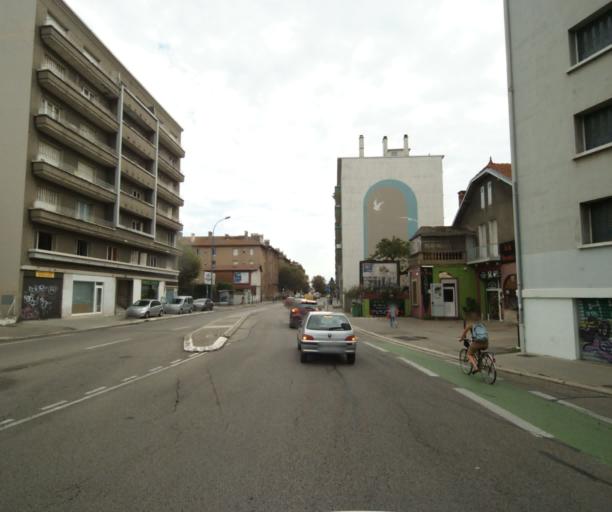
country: FR
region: Rhone-Alpes
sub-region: Departement de l'Isere
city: Grenoble
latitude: 45.1767
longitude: 5.7263
